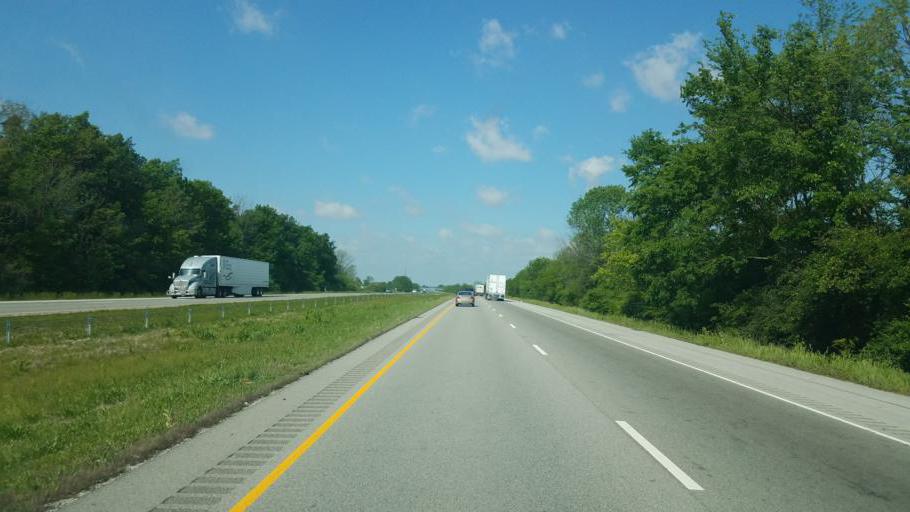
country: US
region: Indiana
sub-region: Morgan County
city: Monrovia
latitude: 39.5868
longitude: -86.5710
